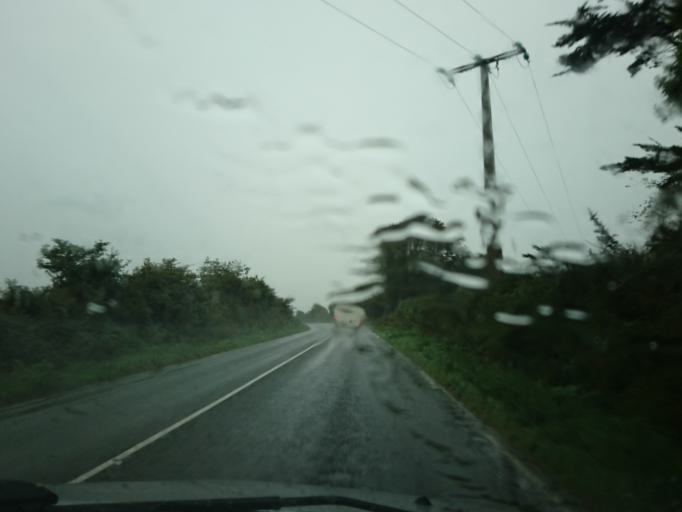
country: FR
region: Brittany
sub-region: Departement du Finistere
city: Gouesnou
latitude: 48.4688
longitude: -4.4449
